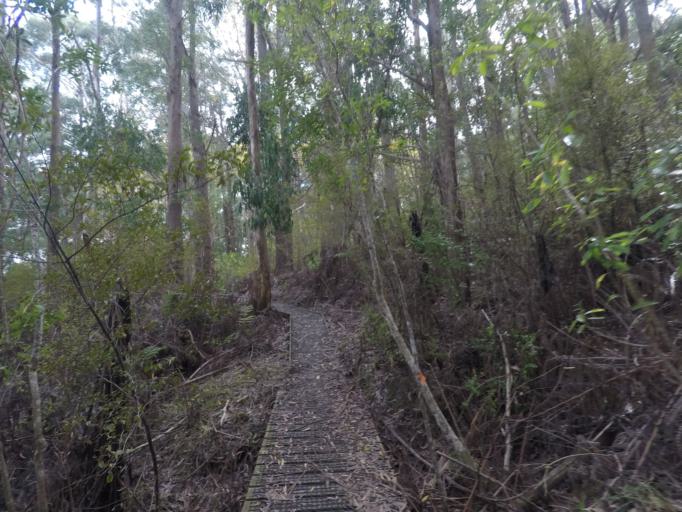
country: NZ
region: Auckland
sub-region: Auckland
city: Rothesay Bay
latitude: -36.6558
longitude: 174.7252
